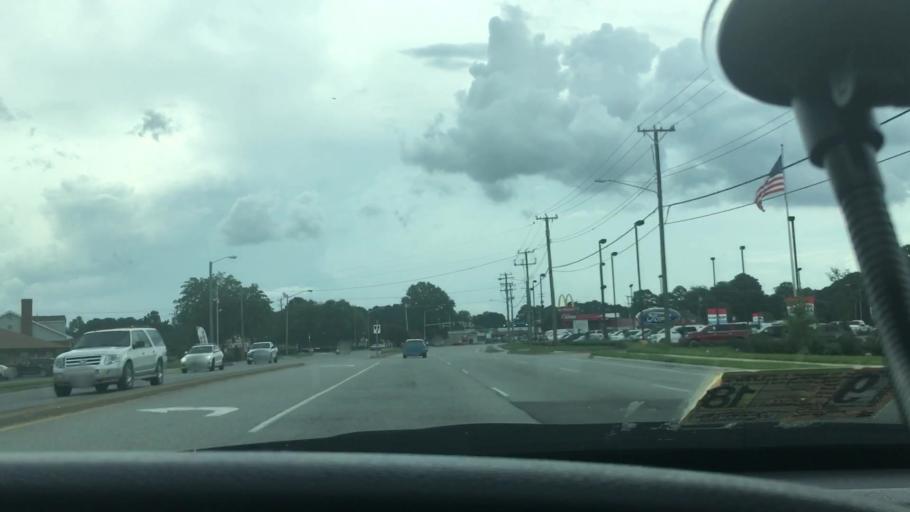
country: US
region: Virginia
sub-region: City of Portsmouth
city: Portsmouth Heights
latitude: 36.8245
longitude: -76.4081
